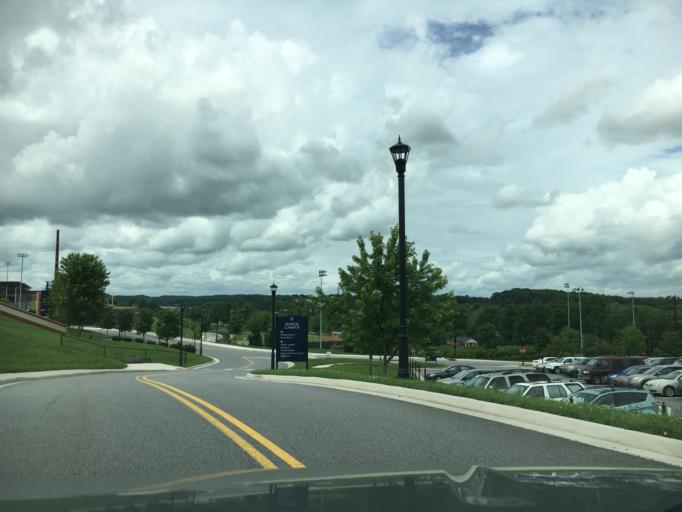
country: US
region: Virginia
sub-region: City of Lynchburg
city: West Lynchburg
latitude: 37.3591
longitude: -79.1754
